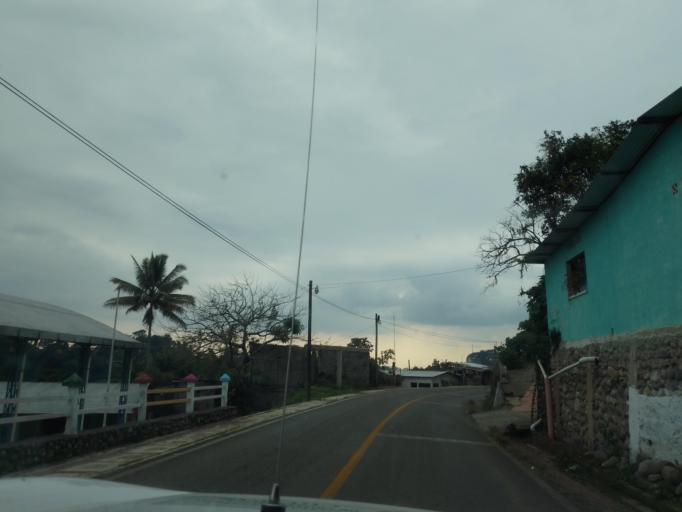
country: MX
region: Chiapas
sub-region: Union Juarez
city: Santo Domingo
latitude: 15.0374
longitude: -92.1190
